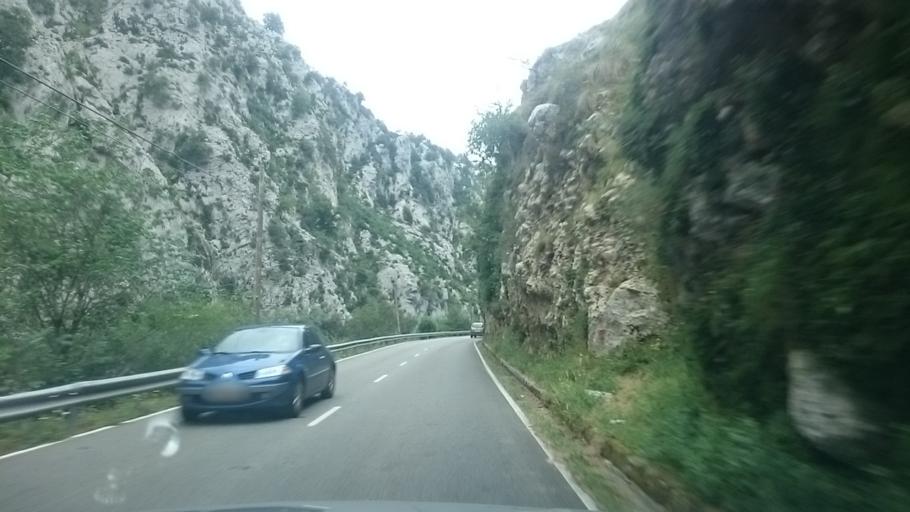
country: ES
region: Asturias
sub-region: Province of Asturias
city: Carrena
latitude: 43.2850
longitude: -4.8336
